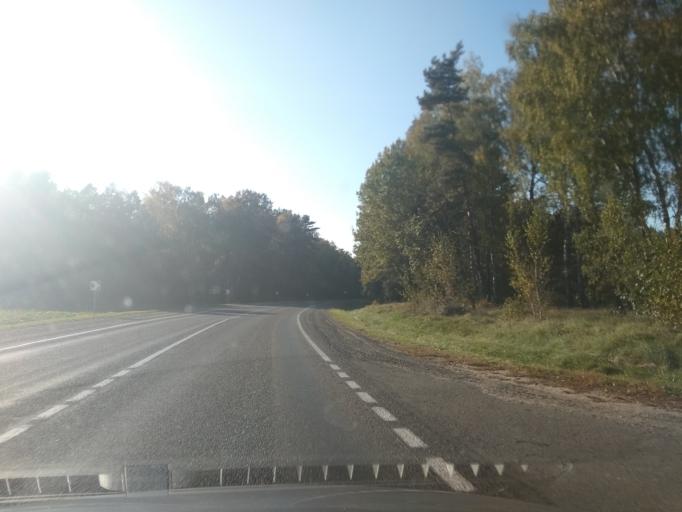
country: BY
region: Grodnenskaya
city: Svislach
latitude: 53.1168
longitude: 24.0692
